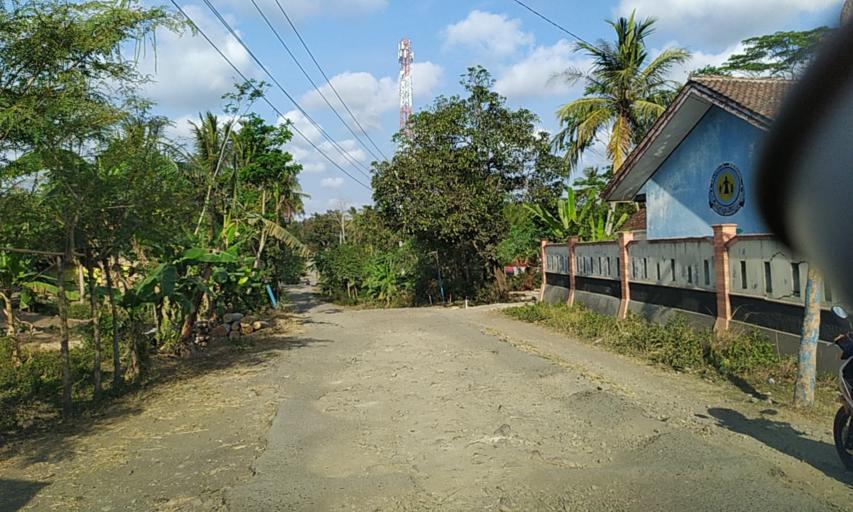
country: ID
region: Central Java
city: Jeruklegi
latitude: -7.6471
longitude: 108.9699
